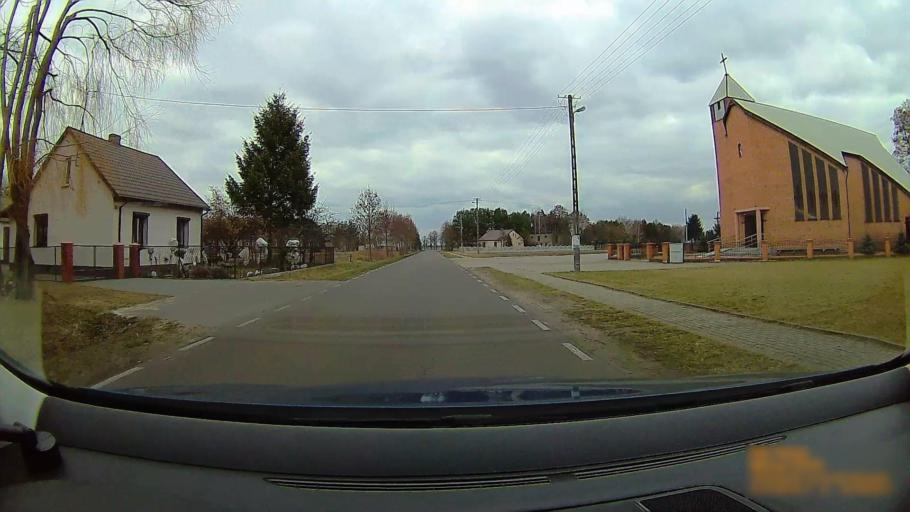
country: PL
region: Greater Poland Voivodeship
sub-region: Powiat koninski
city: Rzgow Pierwszy
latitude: 52.1028
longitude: 18.0940
